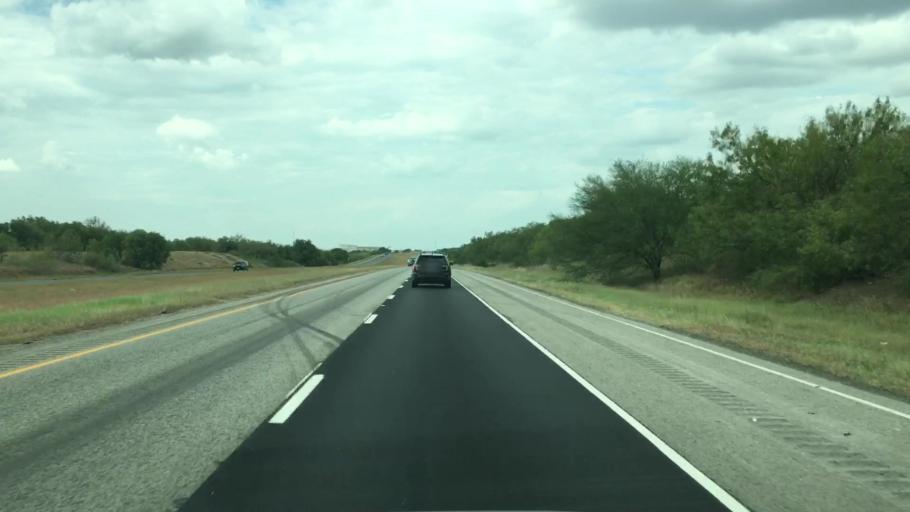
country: US
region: Texas
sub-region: Atascosa County
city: Pleasanton
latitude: 29.0792
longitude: -98.4328
